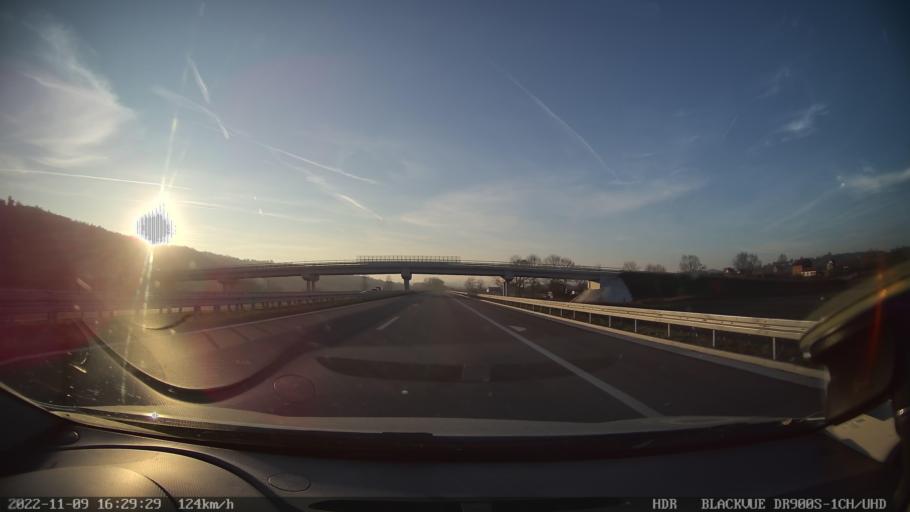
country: RS
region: Central Serbia
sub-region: Moravicki Okrug
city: Cacak
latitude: 43.9242
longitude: 20.3612
